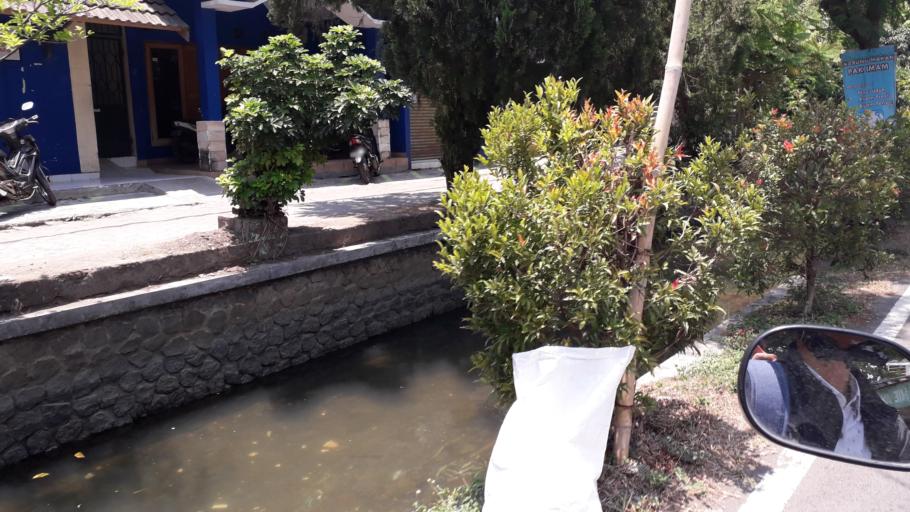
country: ID
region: Daerah Istimewa Yogyakarta
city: Yogyakarta
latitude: -7.7619
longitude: 110.3731
